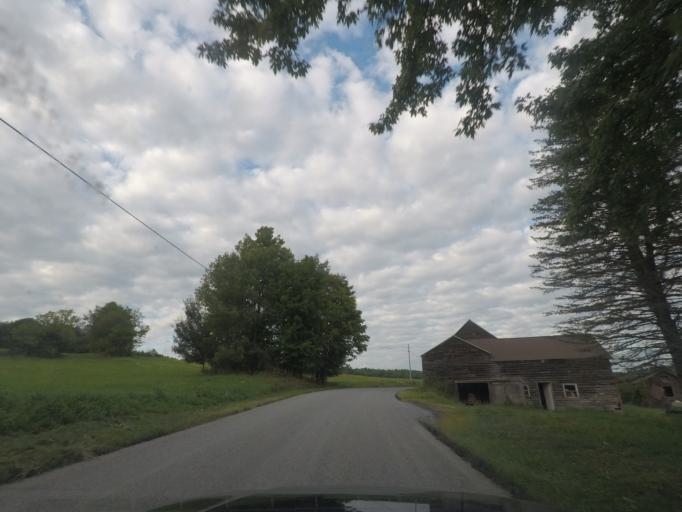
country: US
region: New York
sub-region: Rensselaer County
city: Nassau
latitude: 42.4870
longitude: -73.5924
